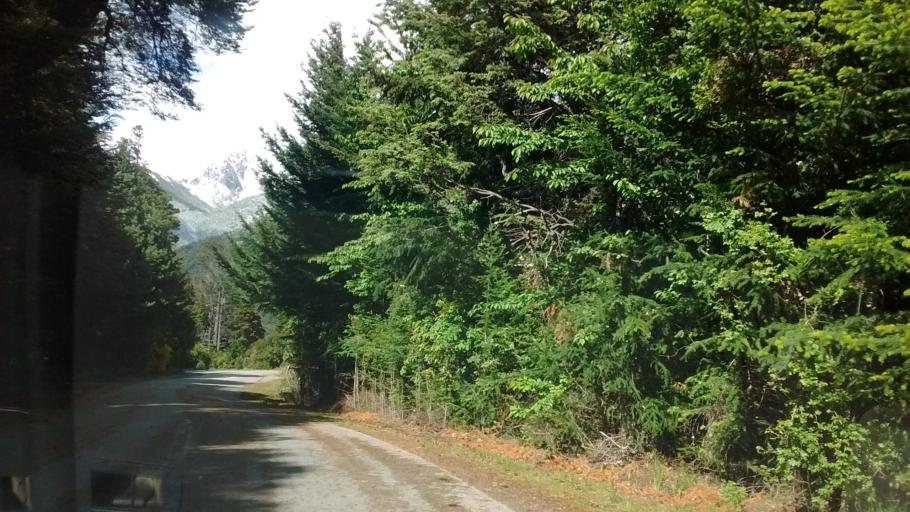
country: AR
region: Rio Negro
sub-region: Departamento de Bariloche
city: San Carlos de Bariloche
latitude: -41.0716
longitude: -71.5446
